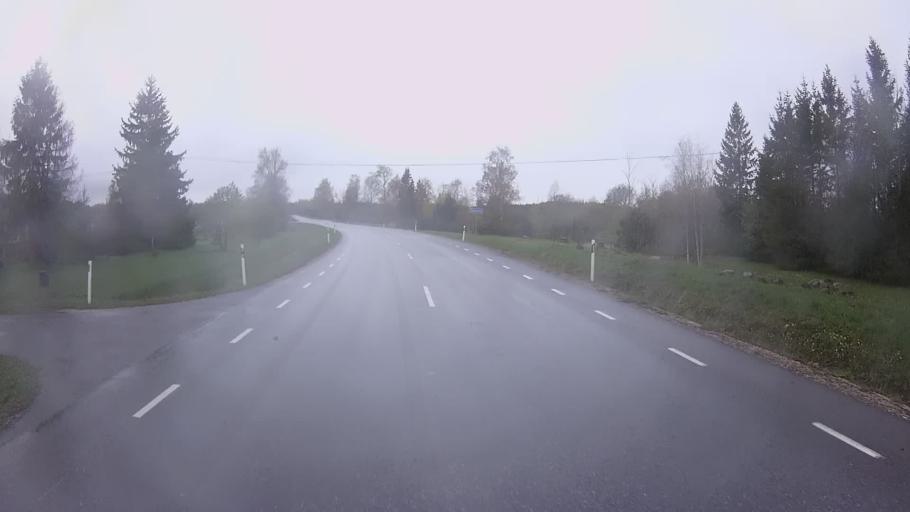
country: EE
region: Hiiumaa
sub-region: Kaerdla linn
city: Kardla
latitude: 58.9922
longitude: 22.5212
